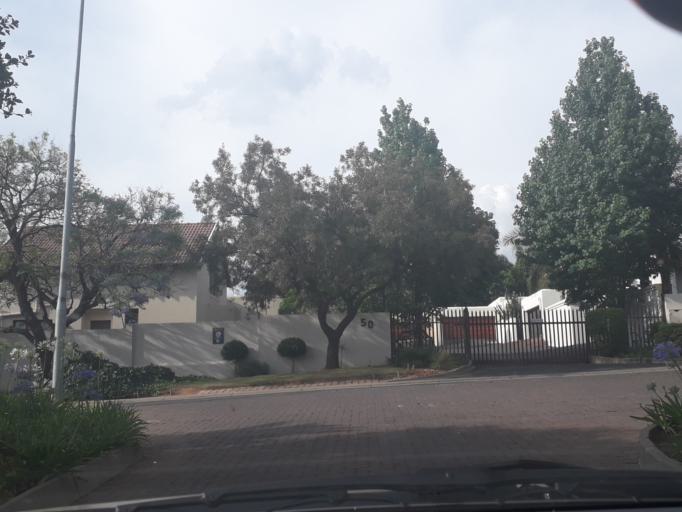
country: ZA
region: Gauteng
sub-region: City of Johannesburg Metropolitan Municipality
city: Diepsloot
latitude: -26.0441
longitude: 28.0015
